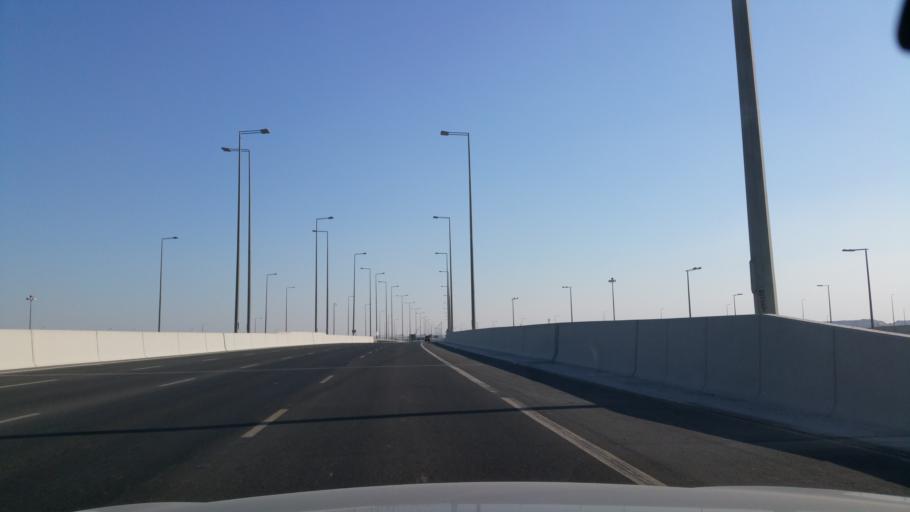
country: QA
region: Al Wakrah
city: Al Wukayr
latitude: 25.1669
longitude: 51.4717
